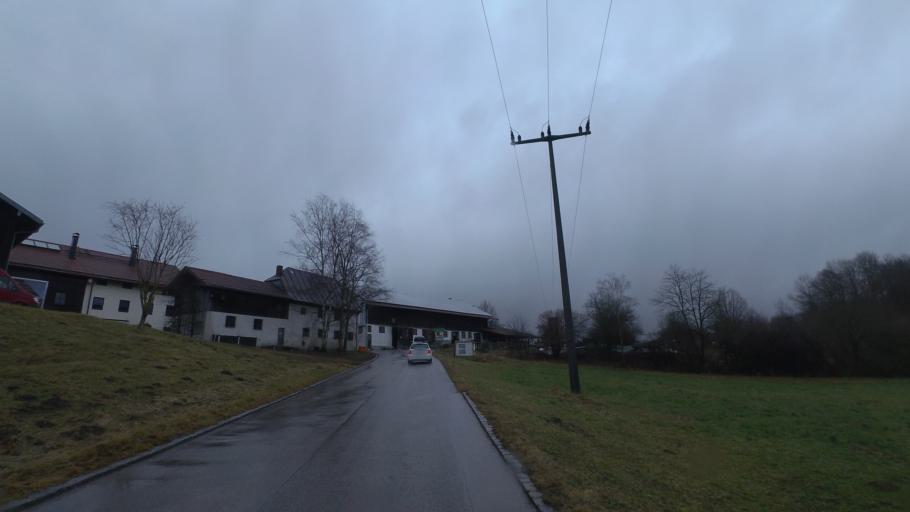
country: DE
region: Bavaria
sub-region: Upper Bavaria
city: Nussdorf
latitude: 47.9201
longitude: 12.6344
